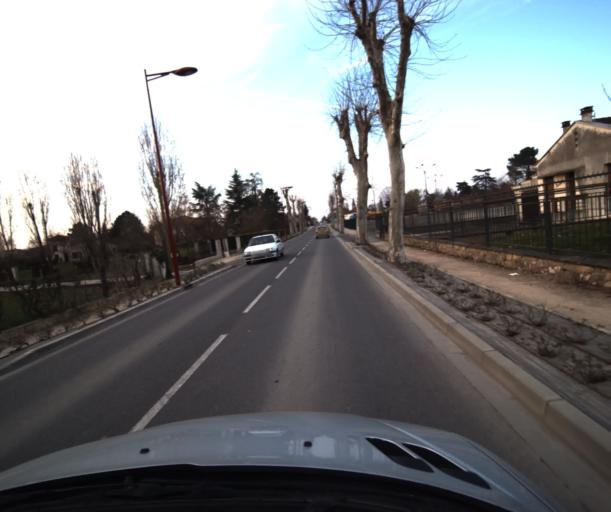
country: FR
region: Midi-Pyrenees
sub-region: Departement du Tarn-et-Garonne
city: Labastide-Saint-Pierre
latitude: 43.9148
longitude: 1.3683
